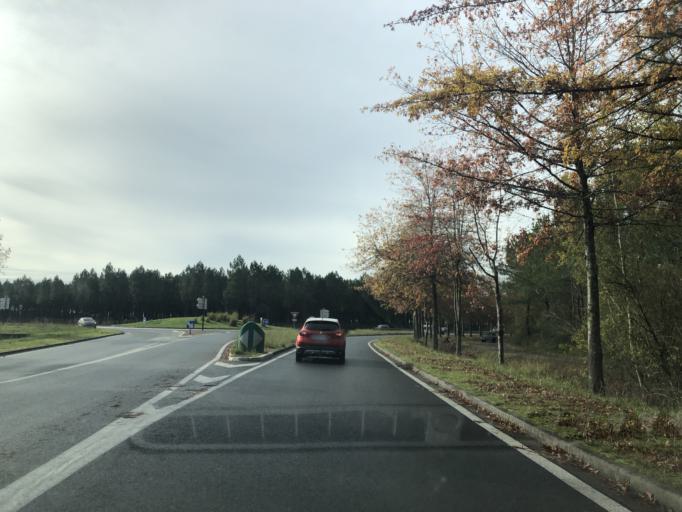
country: FR
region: Aquitaine
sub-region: Departement de la Gironde
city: Marcheprime
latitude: 44.7939
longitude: -0.8742
